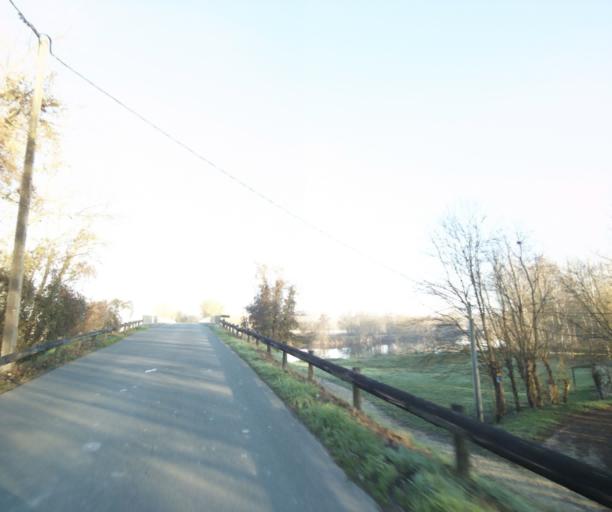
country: FR
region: Poitou-Charentes
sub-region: Departement de la Charente-Maritime
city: Cherac
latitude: 45.6778
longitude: -0.4624
